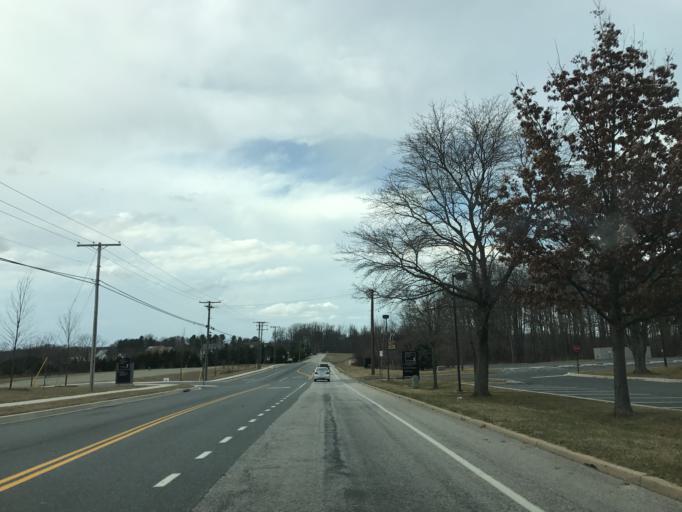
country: US
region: Maryland
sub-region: Harford County
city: South Bel Air
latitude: 39.5637
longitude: -76.2876
